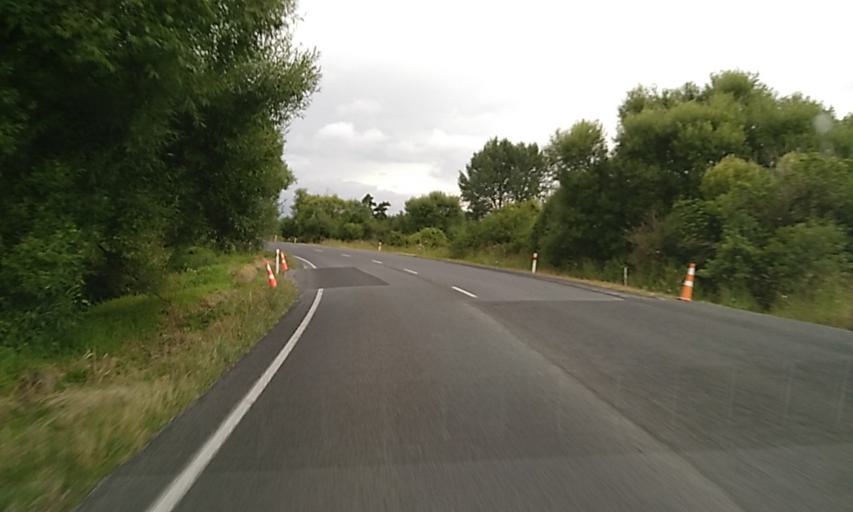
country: NZ
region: Auckland
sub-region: Auckland
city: Pukekohe East
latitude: -37.3043
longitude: 174.9508
